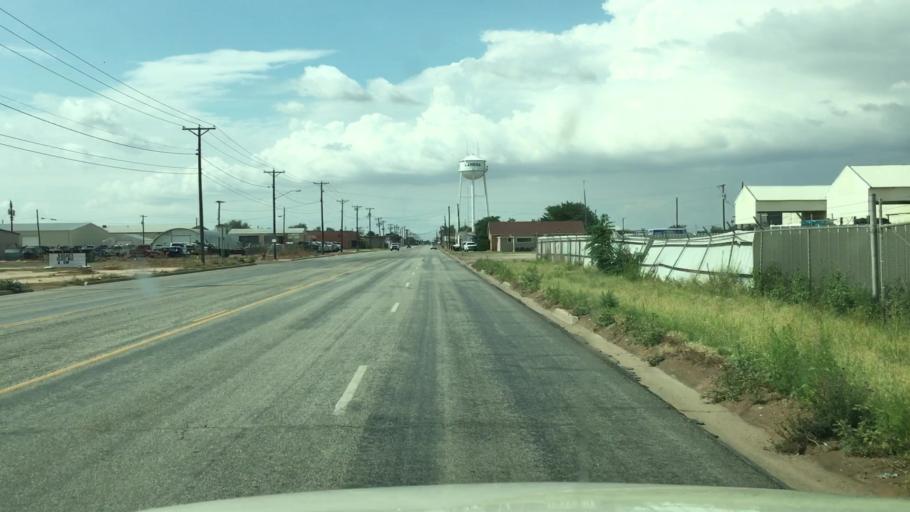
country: US
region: Texas
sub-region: Dawson County
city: Lamesa
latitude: 32.7270
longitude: -101.9472
